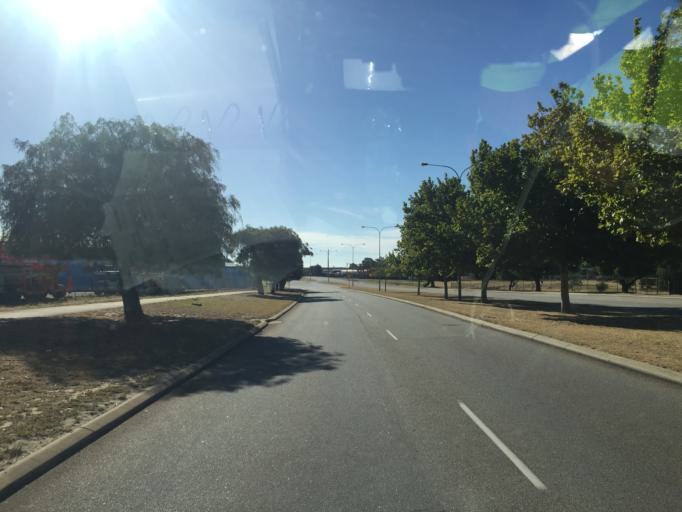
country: AU
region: Western Australia
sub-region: Canning
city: Queens Park
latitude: -31.9961
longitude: 115.9578
